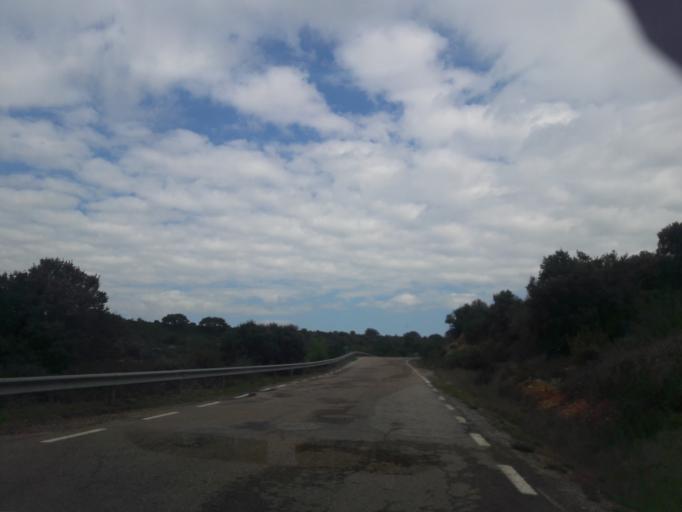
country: ES
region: Castille and Leon
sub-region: Provincia de Salamanca
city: Serradilla del Arroyo
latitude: 40.5281
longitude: -6.3842
